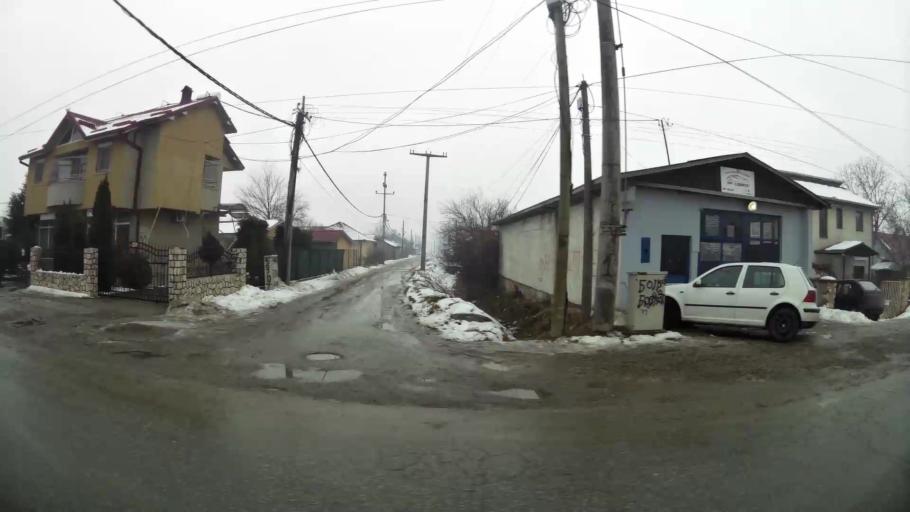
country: MK
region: Petrovec
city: Petrovec
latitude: 41.9292
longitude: 21.6269
